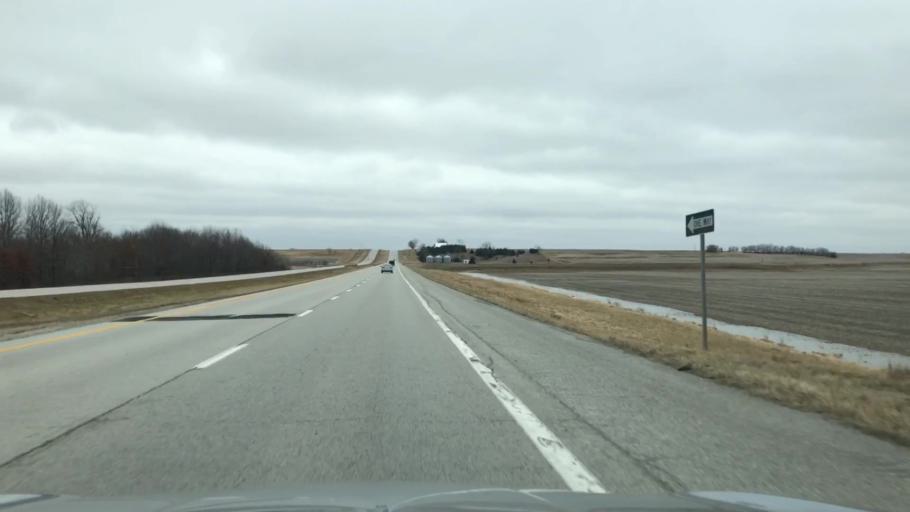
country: US
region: Missouri
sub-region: Livingston County
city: Chillicothe
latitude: 39.7769
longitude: -93.4126
